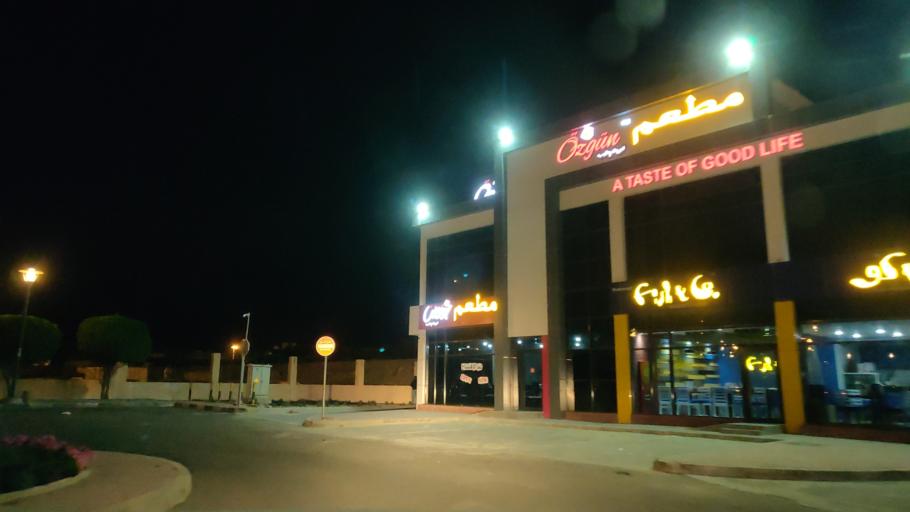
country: KW
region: Al Asimah
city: Ar Rabiyah
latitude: 29.2526
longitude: 47.8429
